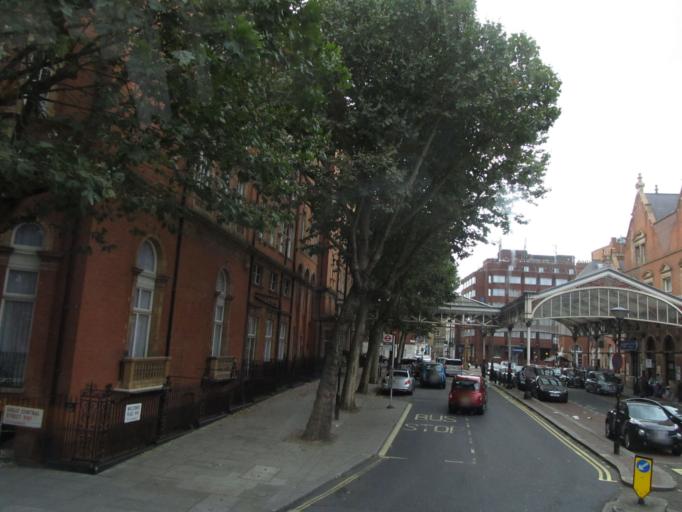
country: GB
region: England
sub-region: Greater London
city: Bayswater
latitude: 51.5223
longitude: -0.1624
